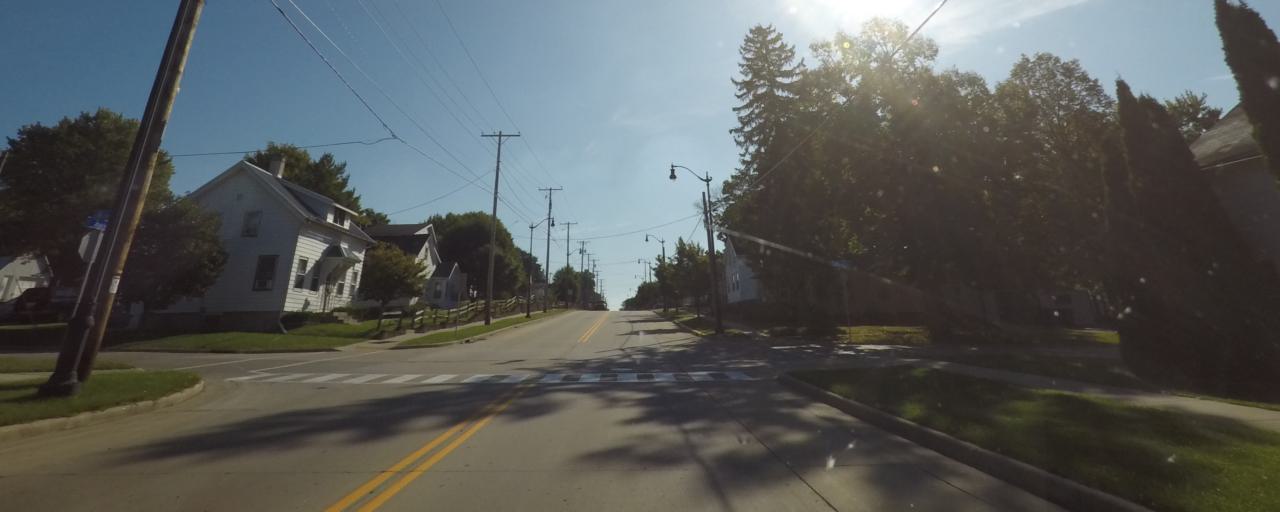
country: US
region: Wisconsin
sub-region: Jefferson County
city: Jefferson
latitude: 43.0051
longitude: -88.8005
